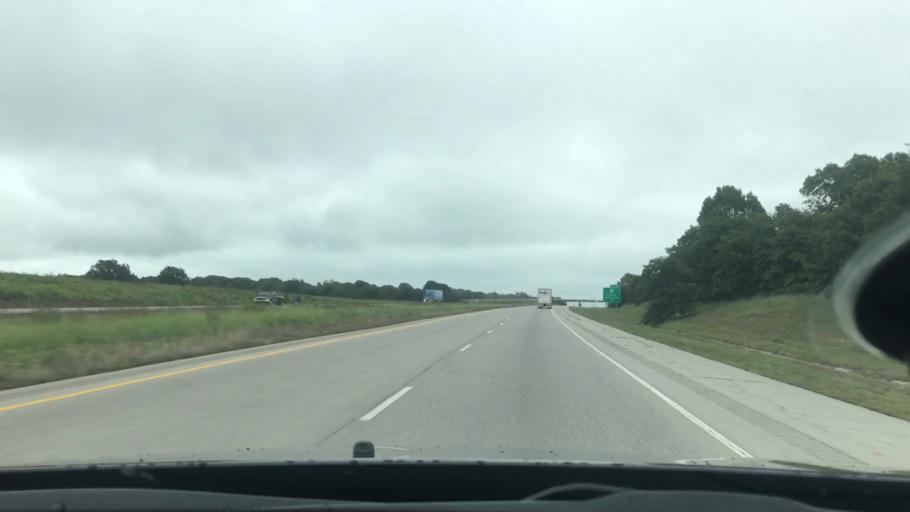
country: US
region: Oklahoma
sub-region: Okfuskee County
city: Okemah
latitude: 35.4004
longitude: -96.3854
